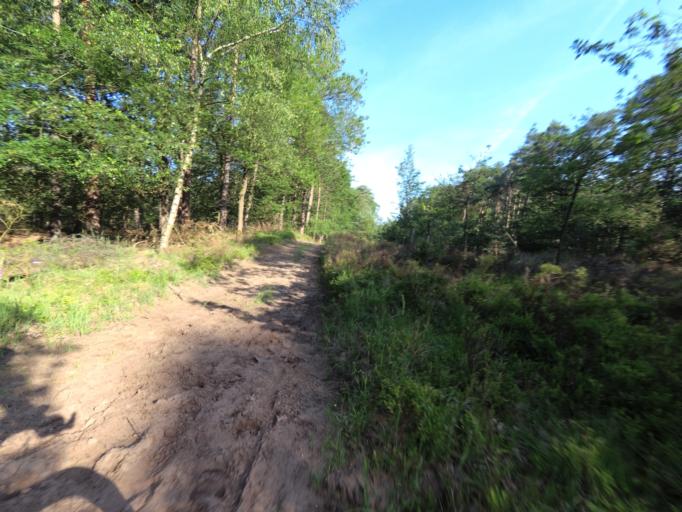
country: NL
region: Gelderland
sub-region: Gemeente Apeldoorn
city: Beekbergen
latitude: 52.1603
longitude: 5.8799
